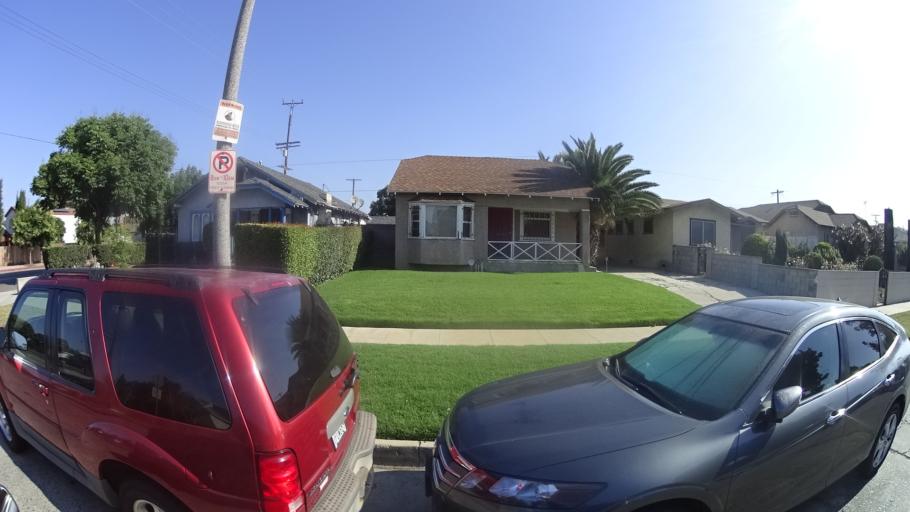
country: US
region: California
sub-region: Los Angeles County
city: Westmont
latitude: 33.9762
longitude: -118.3000
